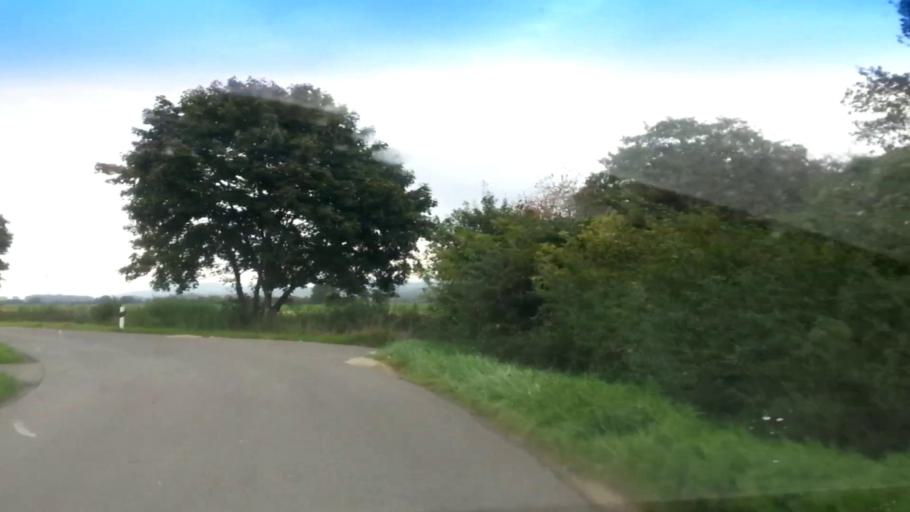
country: DE
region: Bavaria
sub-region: Upper Franconia
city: Rattelsdorf
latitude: 50.0210
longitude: 10.9100
